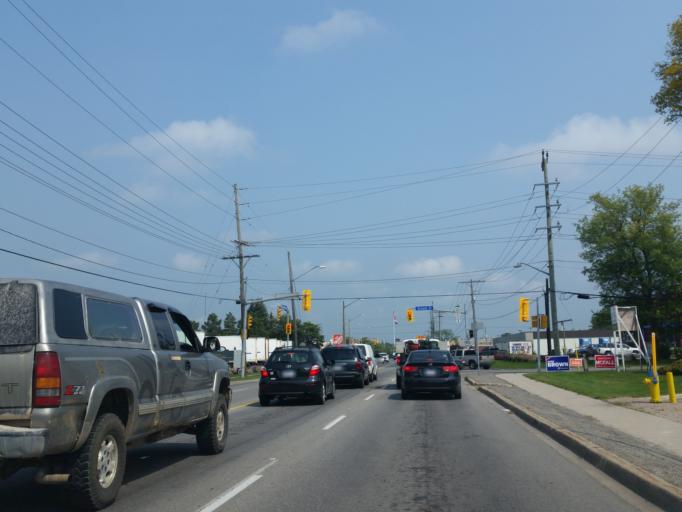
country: CA
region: Ontario
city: Brockville
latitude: 44.6086
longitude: -75.6930
